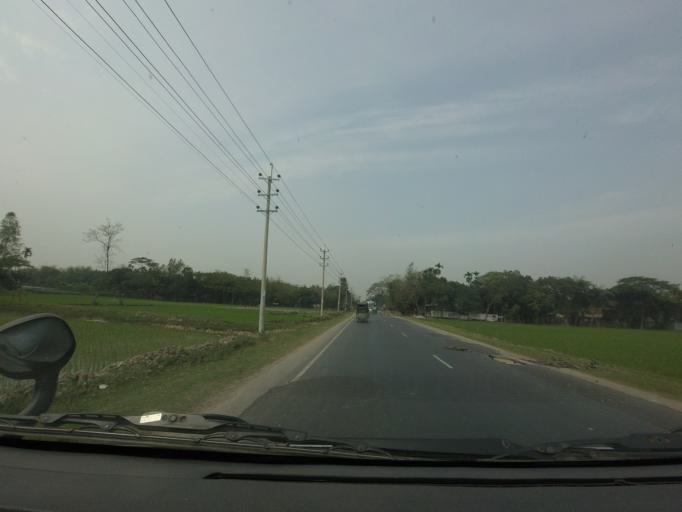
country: BD
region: Dhaka
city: Bajitpur
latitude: 24.2158
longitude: 90.8496
